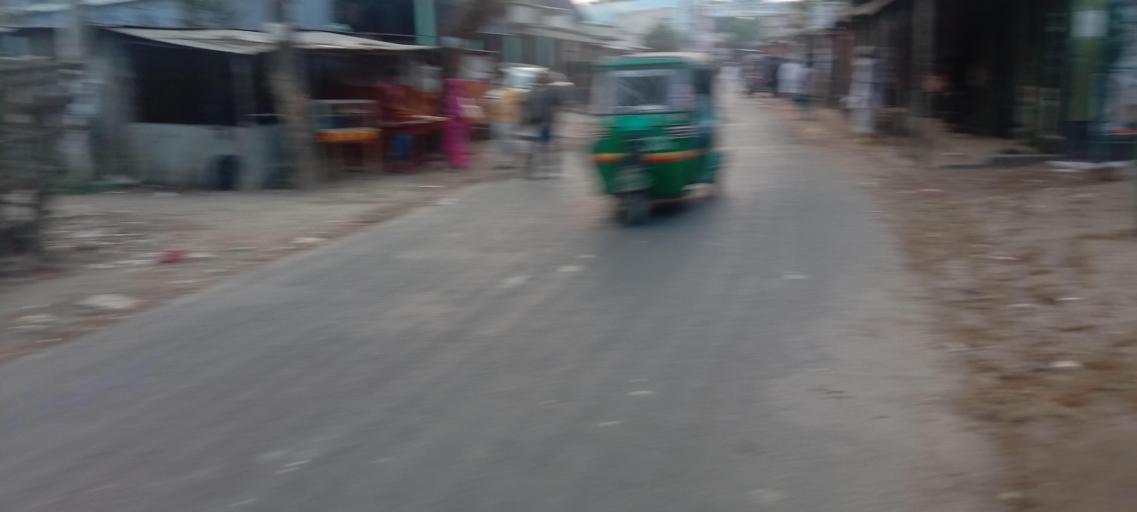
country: BD
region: Dhaka
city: Azimpur
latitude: 23.7335
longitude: 90.2599
